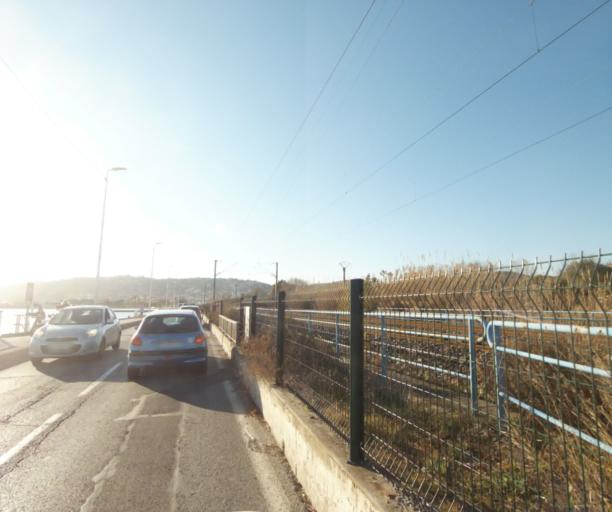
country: FR
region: Provence-Alpes-Cote d'Azur
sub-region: Departement des Alpes-Maritimes
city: Vallauris
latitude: 43.5706
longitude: 7.0906
